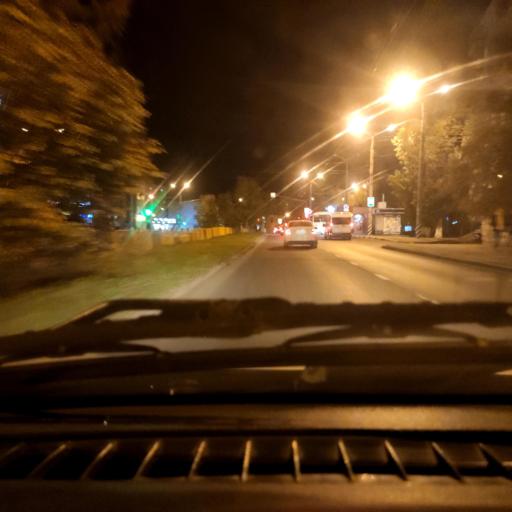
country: RU
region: Samara
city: Zhigulevsk
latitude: 53.4777
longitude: 49.4738
